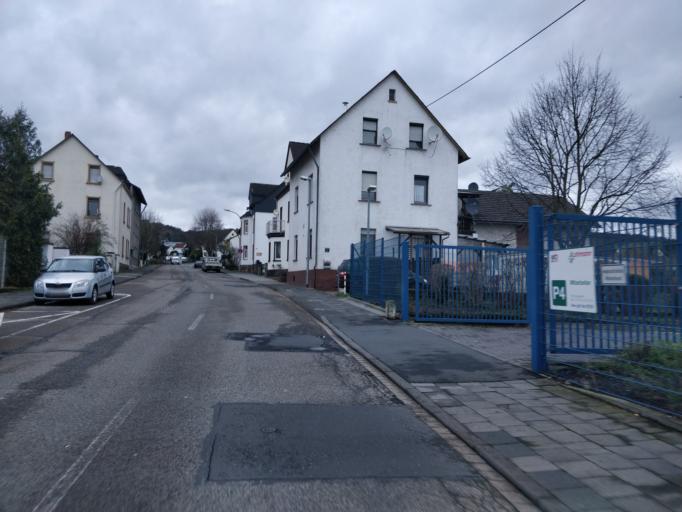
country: DE
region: Rheinland-Pfalz
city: Andernach
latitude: 50.4492
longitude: 7.4294
